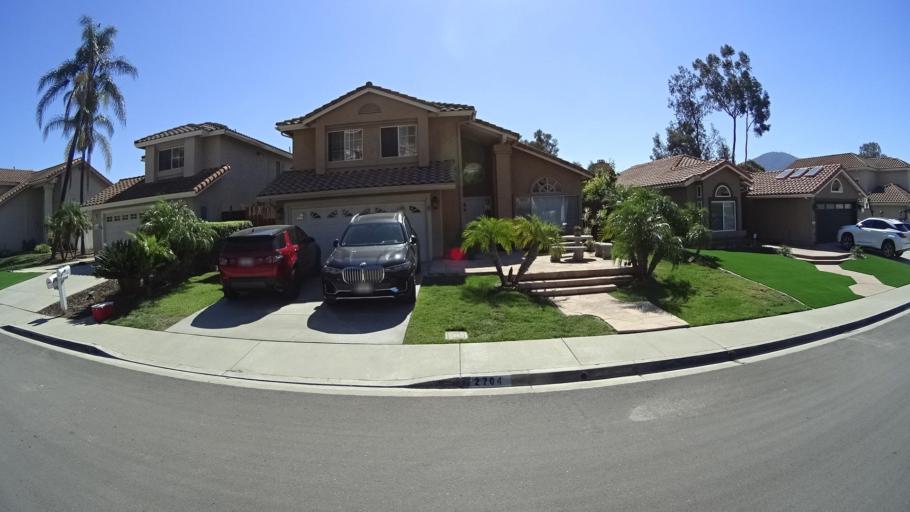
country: US
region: California
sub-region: San Diego County
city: Rancho San Diego
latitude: 32.7462
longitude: -116.9172
